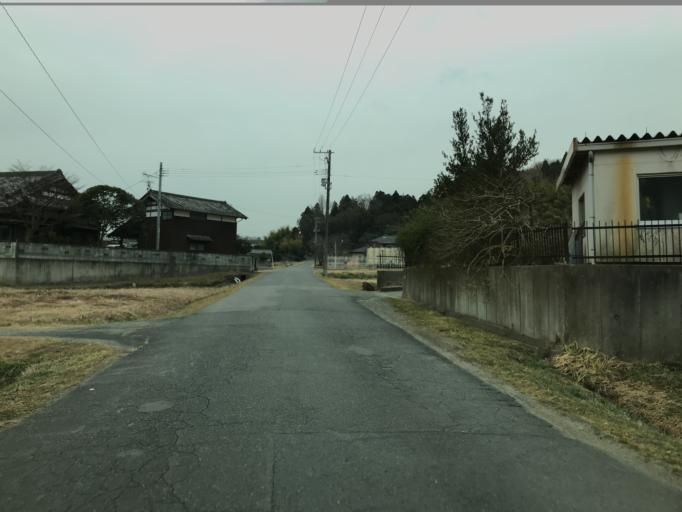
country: JP
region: Fukushima
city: Iwaki
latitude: 37.0698
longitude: 140.8362
